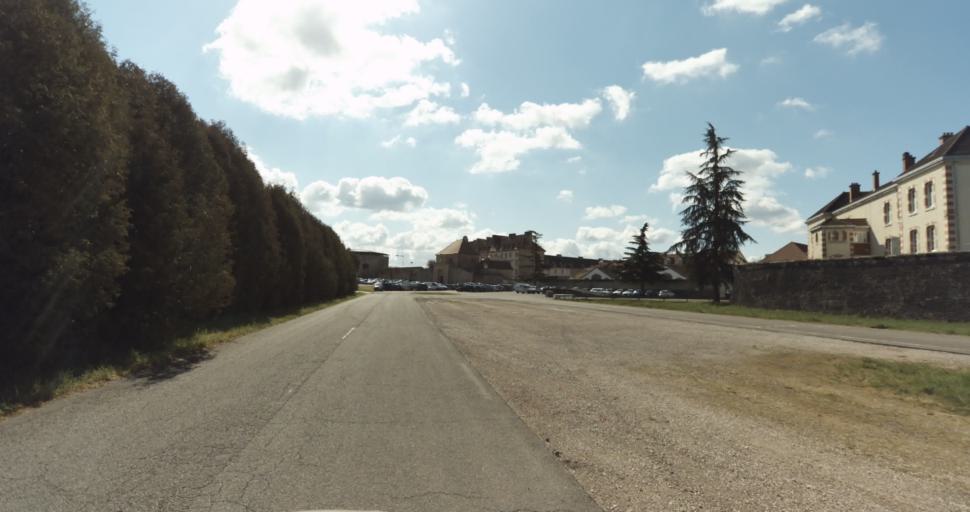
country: FR
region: Bourgogne
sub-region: Departement de la Cote-d'Or
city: Auxonne
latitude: 47.1982
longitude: 5.3899
